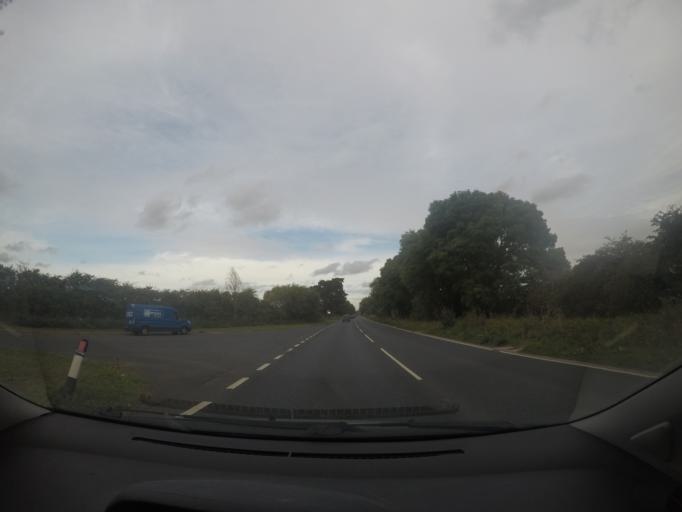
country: GB
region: England
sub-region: City of York
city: Deighton
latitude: 53.8946
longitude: -1.0471
